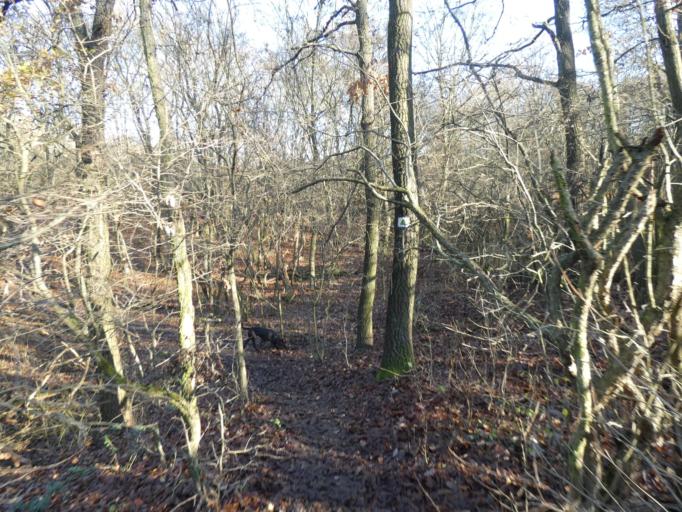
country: HU
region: Pest
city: Paty
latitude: 47.5000
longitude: 18.8463
